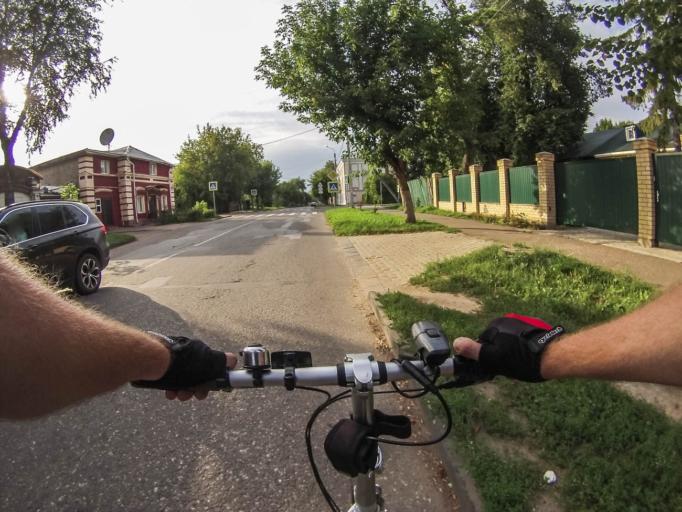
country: RU
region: Kostroma
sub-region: Kostromskoy Rayon
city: Kostroma
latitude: 57.7723
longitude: 40.9128
